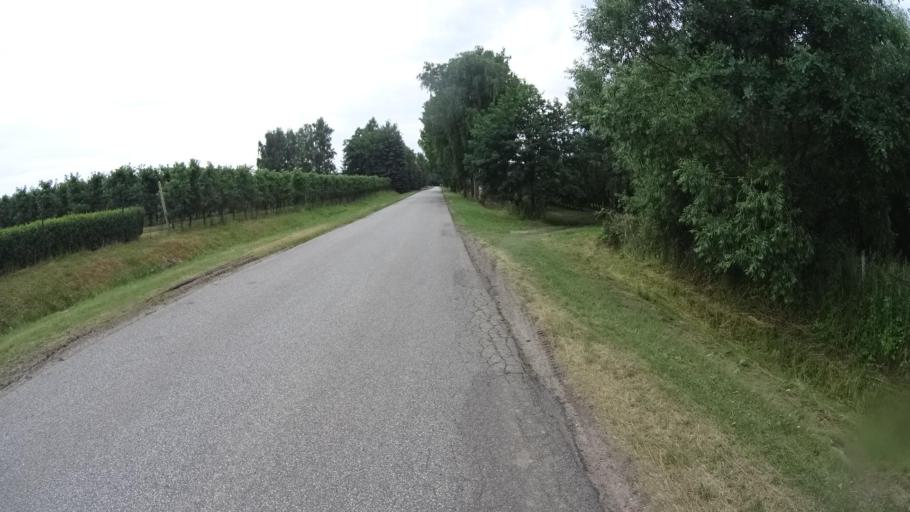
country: PL
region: Masovian Voivodeship
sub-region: Powiat grojecki
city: Goszczyn
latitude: 51.7867
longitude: 20.8554
